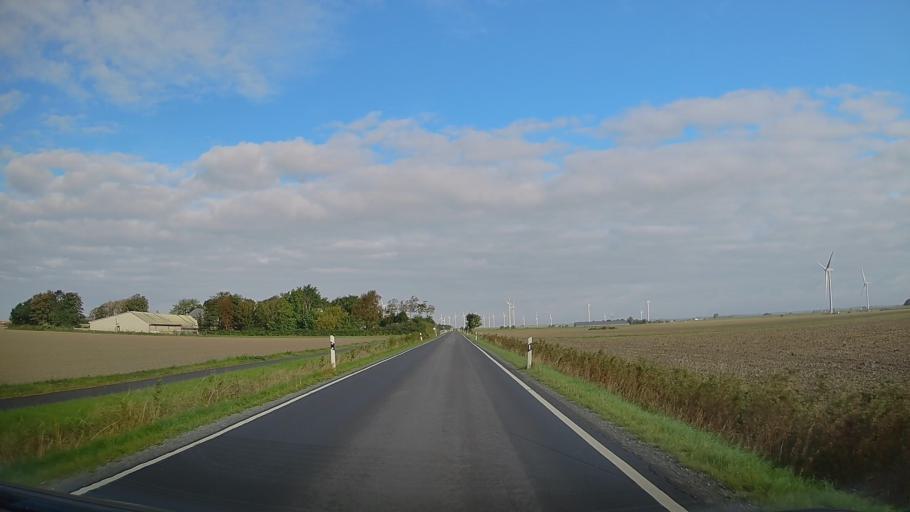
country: DE
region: Schleswig-Holstein
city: Reussenkoge
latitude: 54.5776
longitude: 8.9268
